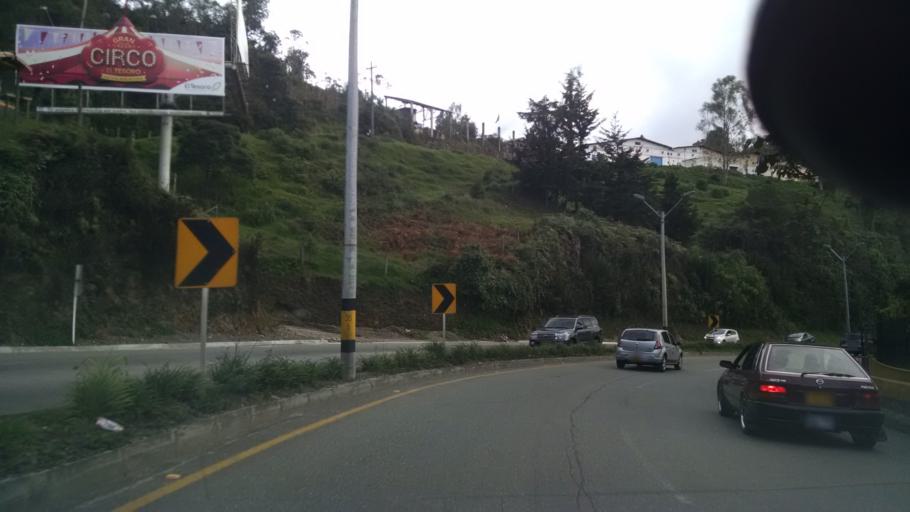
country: CO
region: Antioquia
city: Envigado
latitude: 6.1532
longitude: -75.5433
